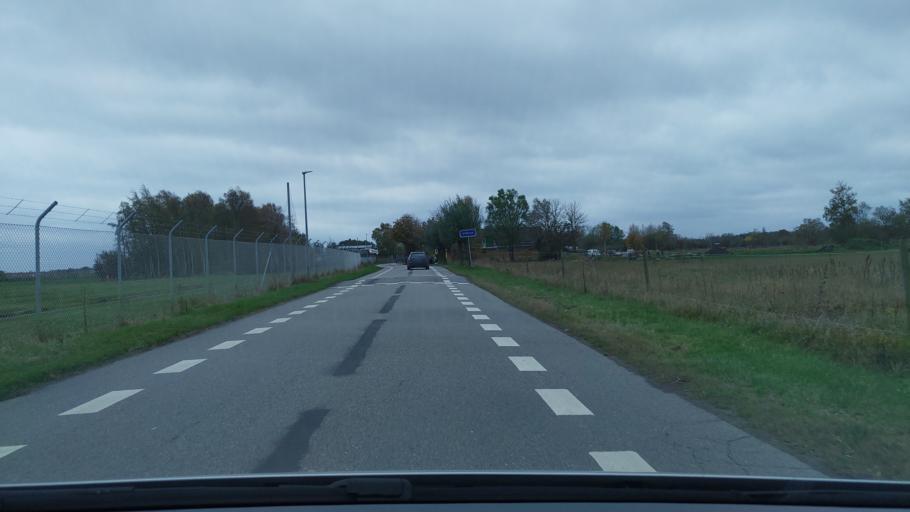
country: DK
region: Capital Region
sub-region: Tarnby Kommune
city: Tarnby
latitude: 55.5953
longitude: 12.5983
